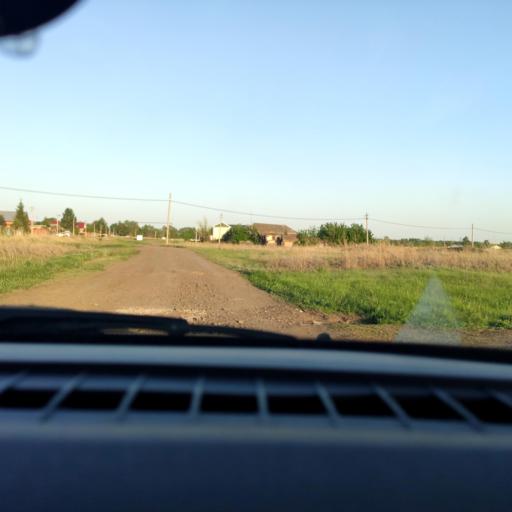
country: RU
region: Samara
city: Georgiyevka
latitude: 53.2765
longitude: 50.9665
